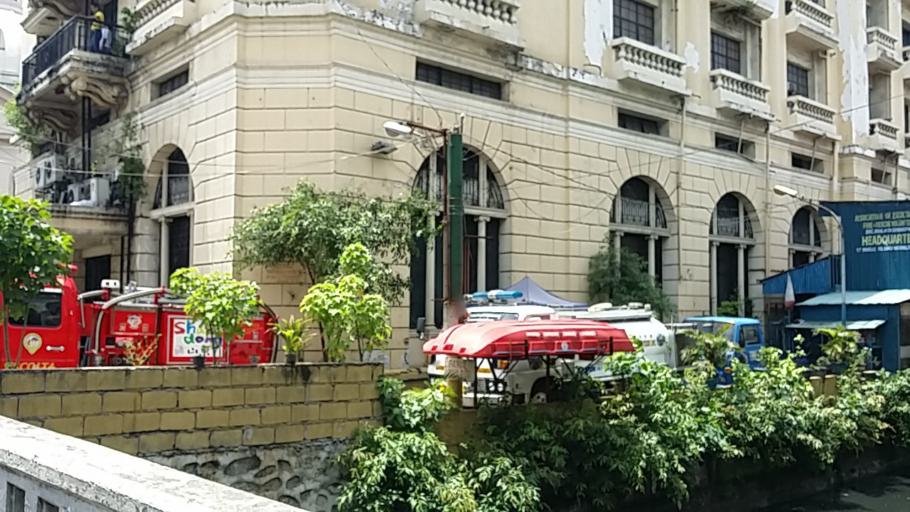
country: PH
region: Metro Manila
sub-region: City of Manila
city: Quiapo
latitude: 14.5990
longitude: 120.9797
